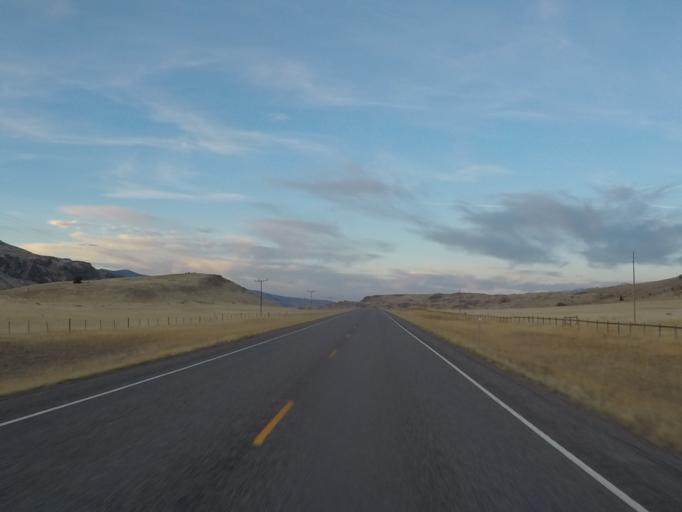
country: US
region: Montana
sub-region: Gallatin County
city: Bozeman
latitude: 45.2180
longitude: -110.8852
